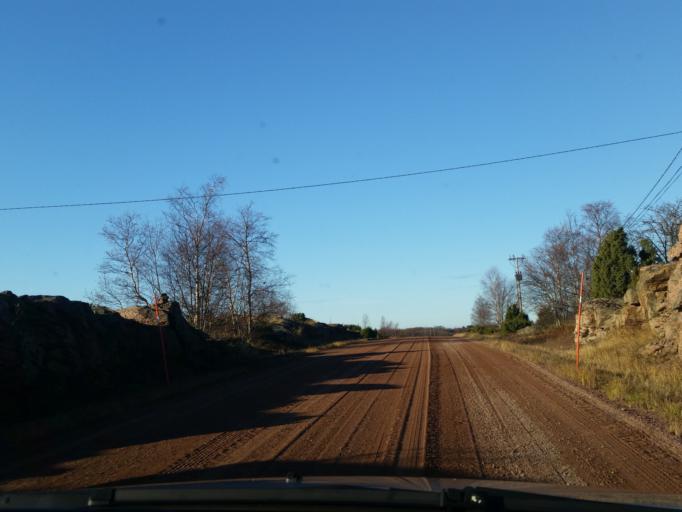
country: AX
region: Alands skaergard
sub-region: Braendoe
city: Braendoe
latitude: 60.4223
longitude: 20.9730
